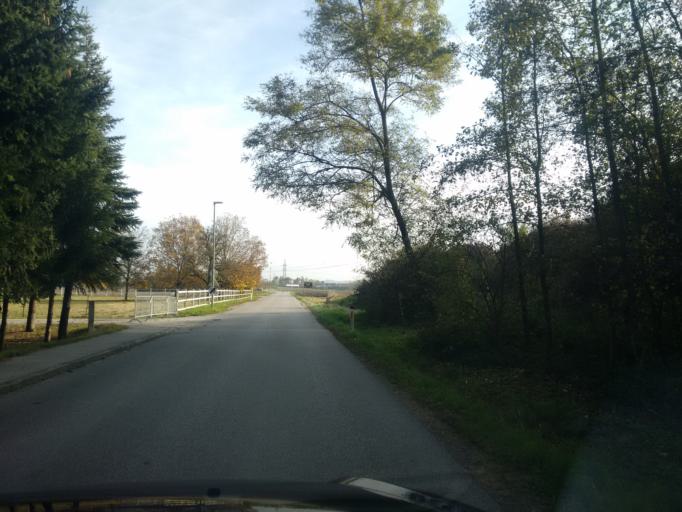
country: AT
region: Upper Austria
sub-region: Wels Stadt
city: Wels
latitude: 48.1863
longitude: 14.0020
